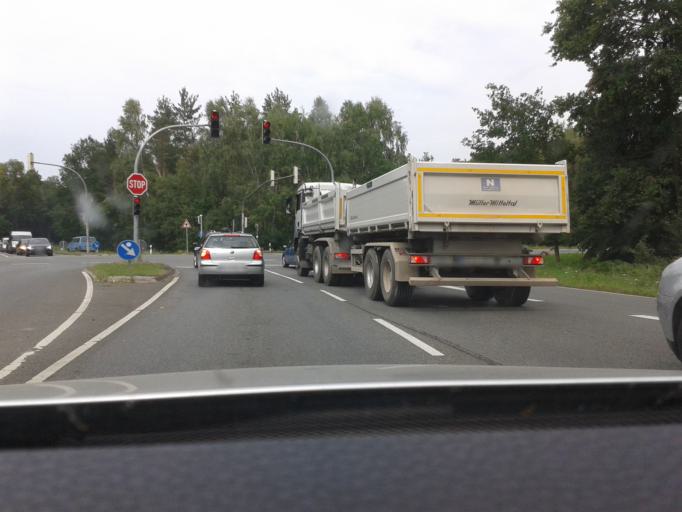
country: DE
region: Lower Saxony
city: Gifhorn
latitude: 52.4962
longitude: 10.5701
